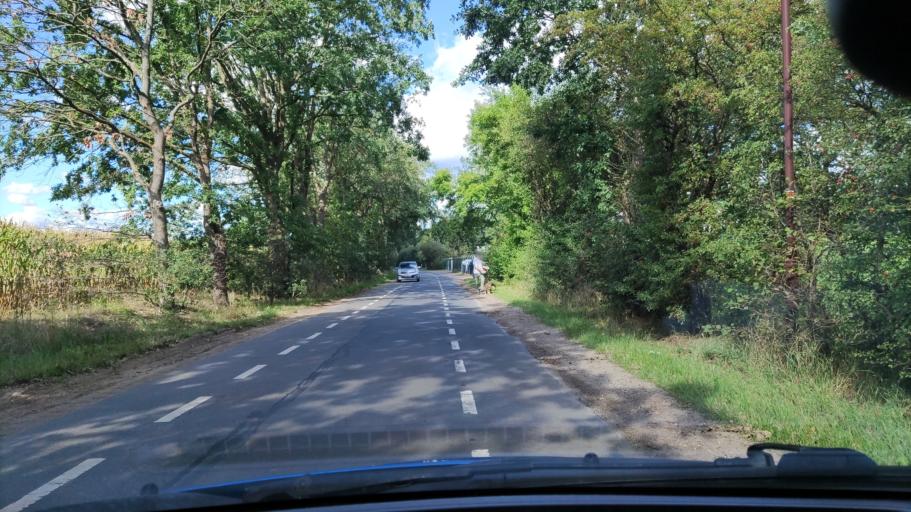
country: DE
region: Lower Saxony
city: Bardowick
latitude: 53.2998
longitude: 10.3751
